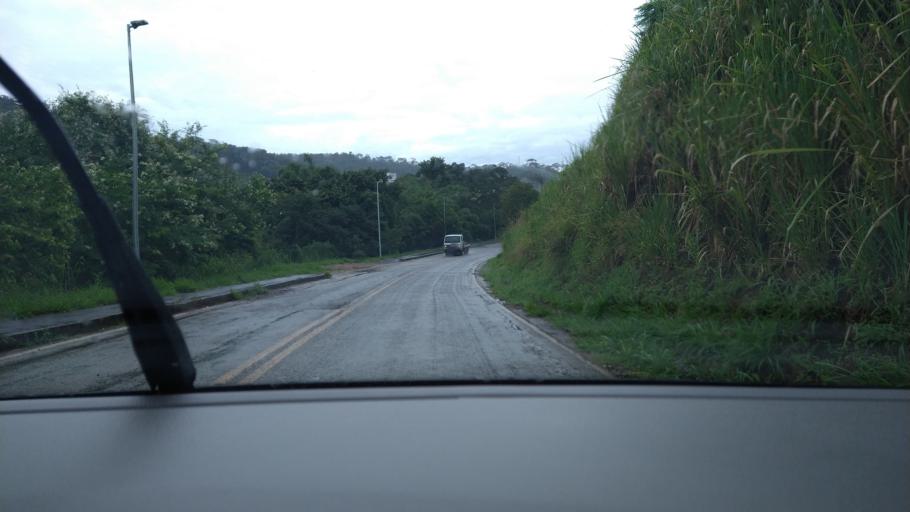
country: BR
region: Minas Gerais
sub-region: Ponte Nova
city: Ponte Nova
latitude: -20.3859
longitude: -42.9016
